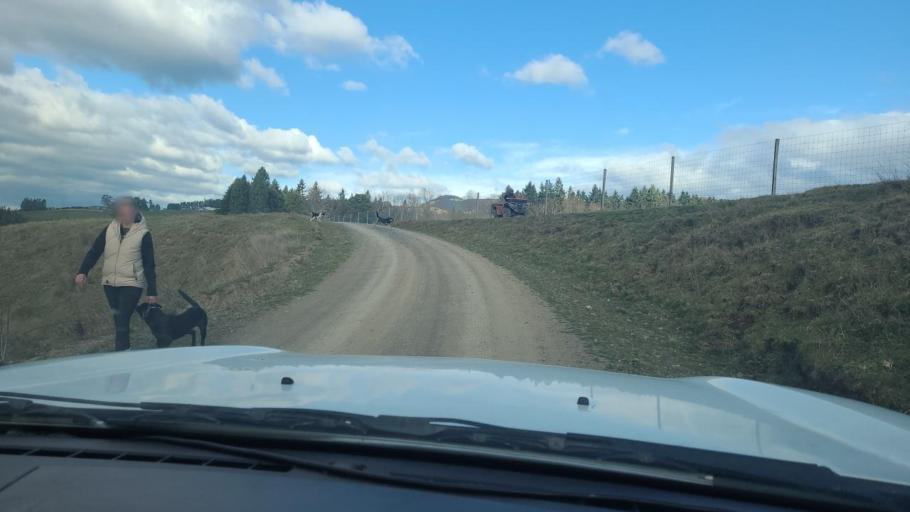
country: NZ
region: Hawke's Bay
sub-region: Hastings District
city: Hastings
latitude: -39.6381
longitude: 176.3885
